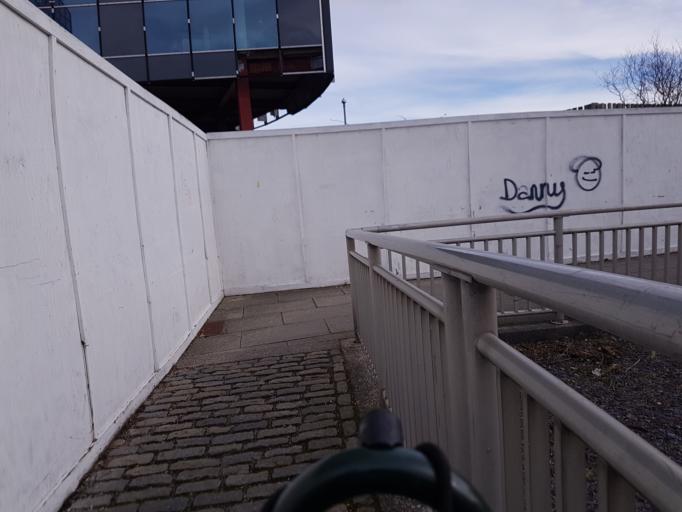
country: GB
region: England
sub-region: Metropolitan Borough of Wirral
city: New Ferry
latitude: 53.3789
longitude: -2.9734
